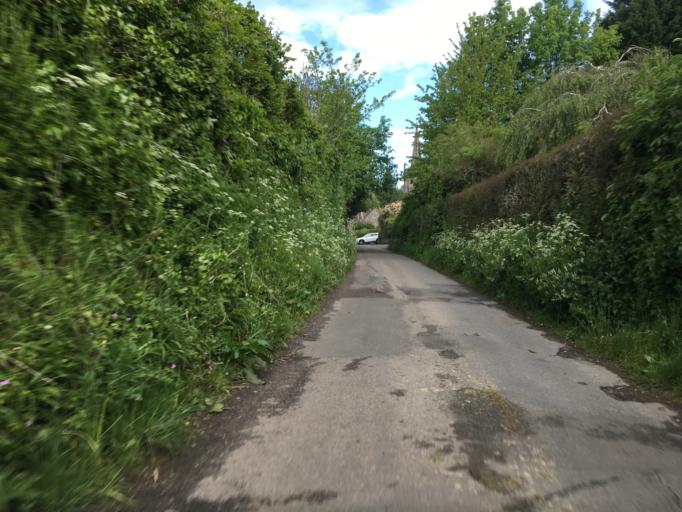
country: GB
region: England
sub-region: Gloucestershire
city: Dursley
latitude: 51.6863
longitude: -2.3933
